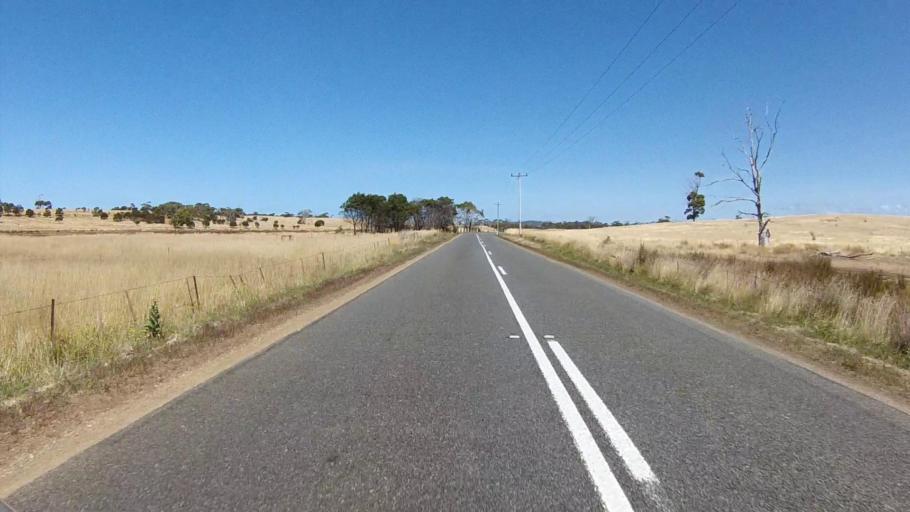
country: AU
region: Tasmania
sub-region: Sorell
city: Sorell
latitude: -42.2747
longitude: 148.0042
